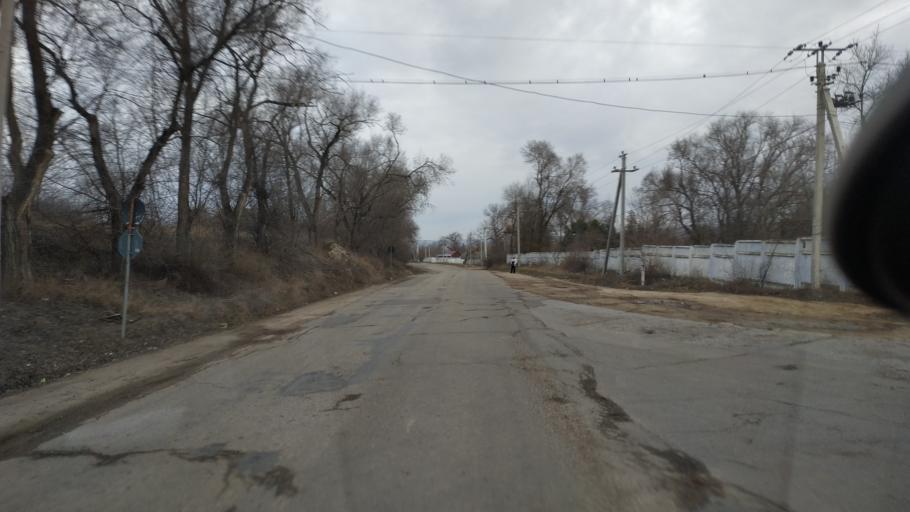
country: MD
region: Criuleni
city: Criuleni
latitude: 47.2363
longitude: 29.1544
